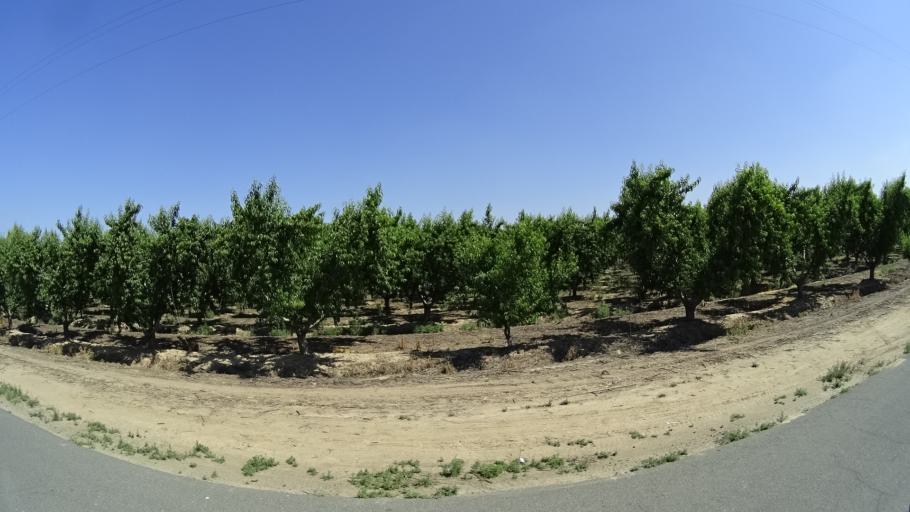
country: US
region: California
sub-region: Fresno County
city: Kingsburg
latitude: 36.4596
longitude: -119.5787
